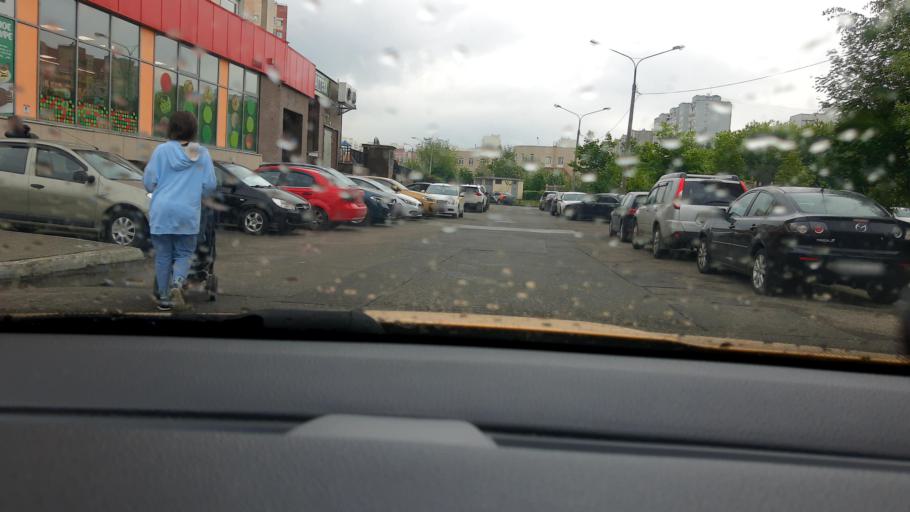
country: RU
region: Moscow
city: Vatutino
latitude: 55.9029
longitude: 37.6991
